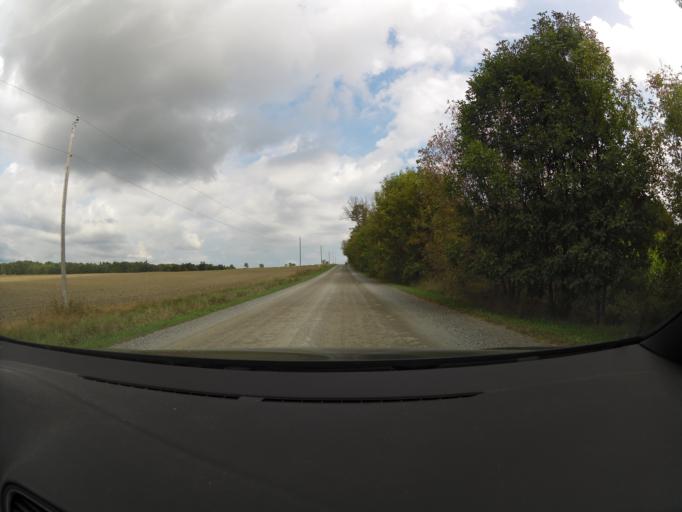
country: CA
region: Ontario
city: Arnprior
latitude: 45.3984
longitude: -76.2375
